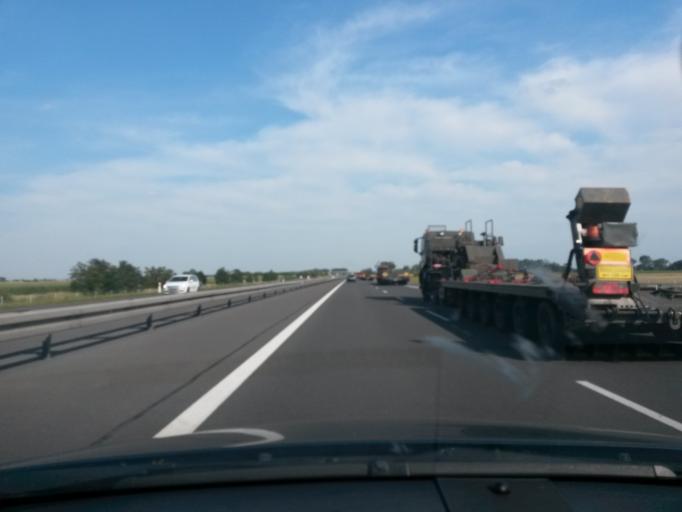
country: PL
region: Greater Poland Voivodeship
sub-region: Powiat wrzesinski
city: Wrzesnia
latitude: 52.2981
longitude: 17.6362
